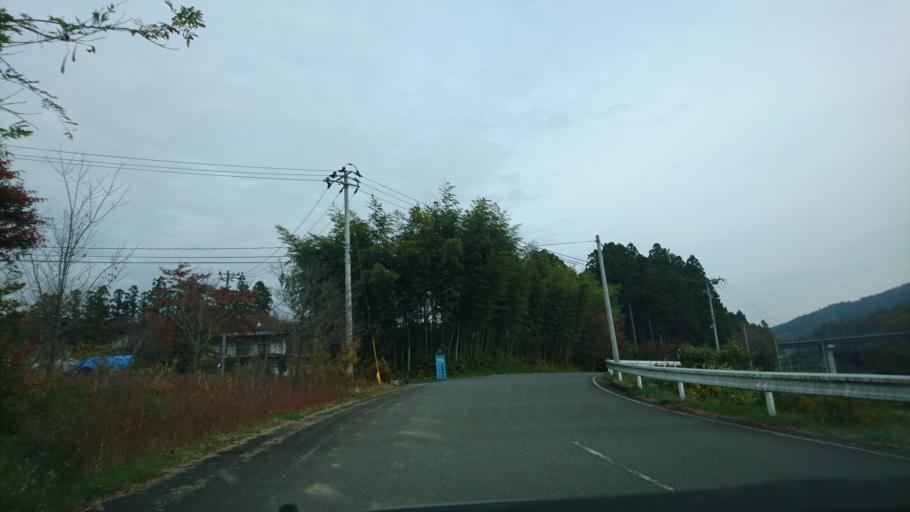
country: JP
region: Iwate
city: Ichinoseki
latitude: 38.9692
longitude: 141.1663
